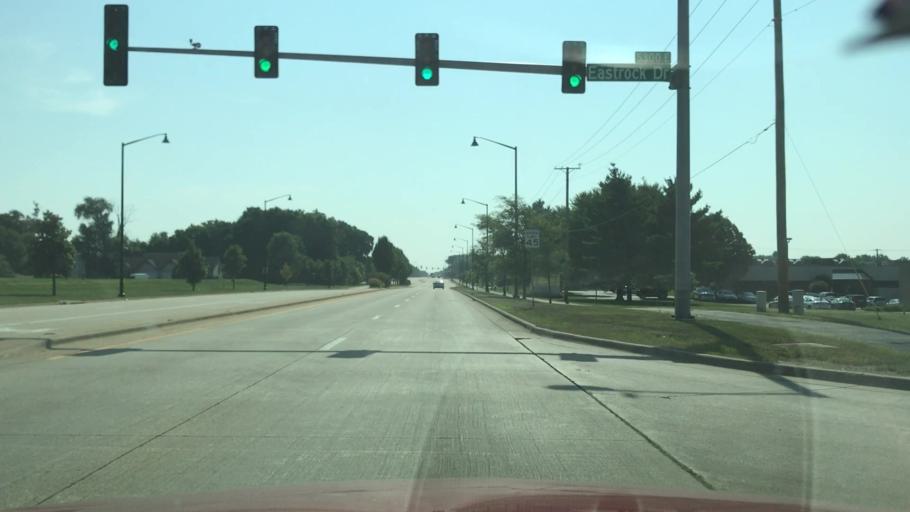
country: US
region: Illinois
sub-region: Winnebago County
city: Cherry Valley
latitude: 42.2383
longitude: -89.0124
